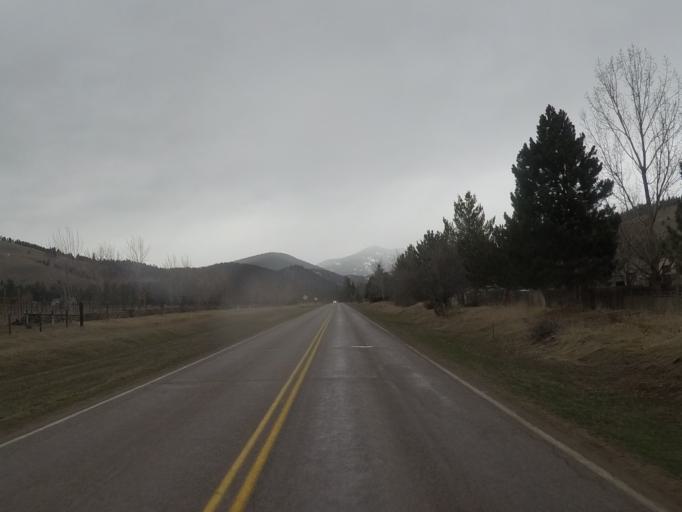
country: US
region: Montana
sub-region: Missoula County
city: East Missoula
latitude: 46.9016
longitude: -113.9604
